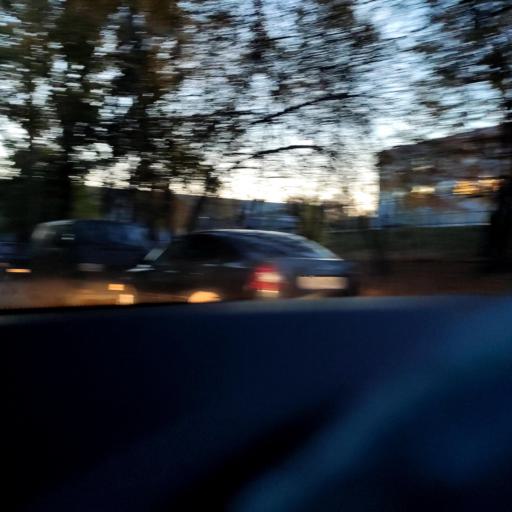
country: RU
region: Samara
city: Samara
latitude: 53.2526
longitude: 50.2426
